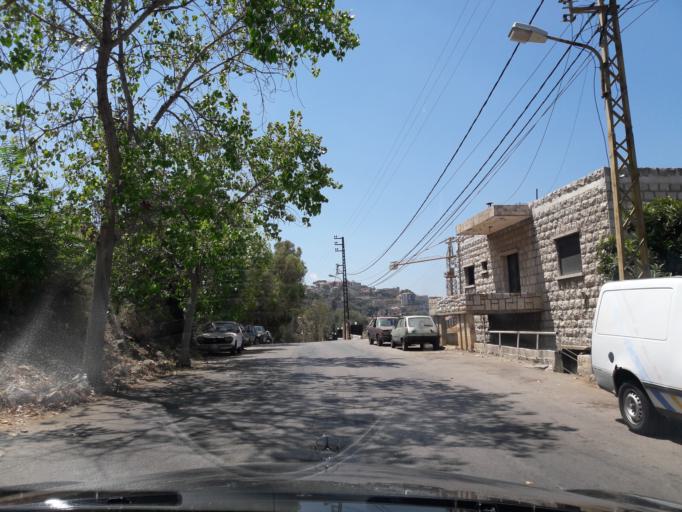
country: LB
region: Mont-Liban
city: Djounie
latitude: 33.9242
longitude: 35.6452
